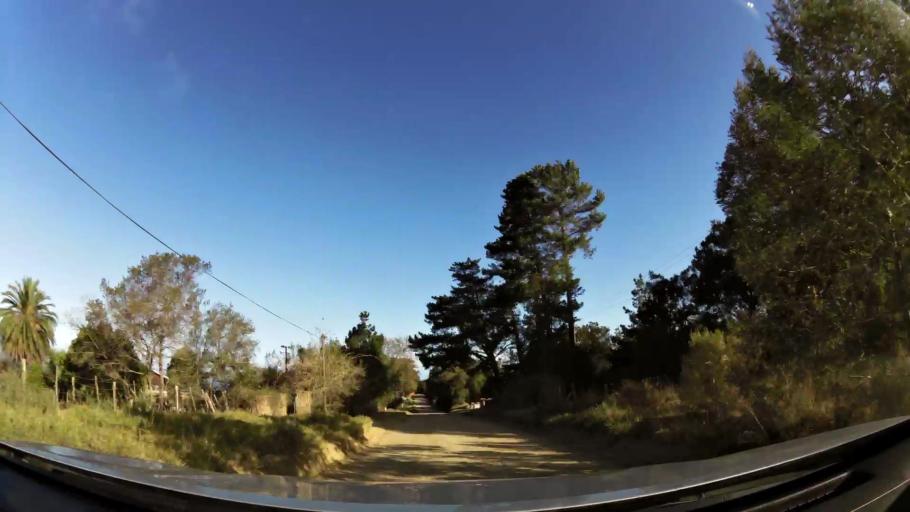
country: ZA
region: Western Cape
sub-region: Eden District Municipality
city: George
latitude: -33.9823
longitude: 22.5686
